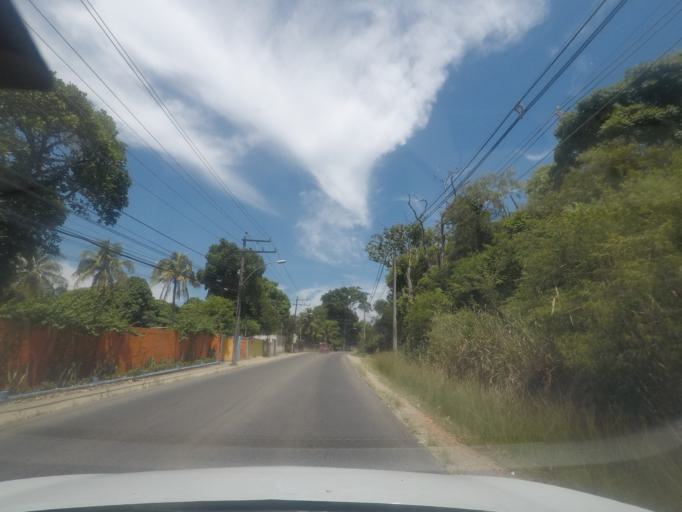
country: BR
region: Rio de Janeiro
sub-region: Itaguai
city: Itaguai
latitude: -22.9851
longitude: -43.6568
